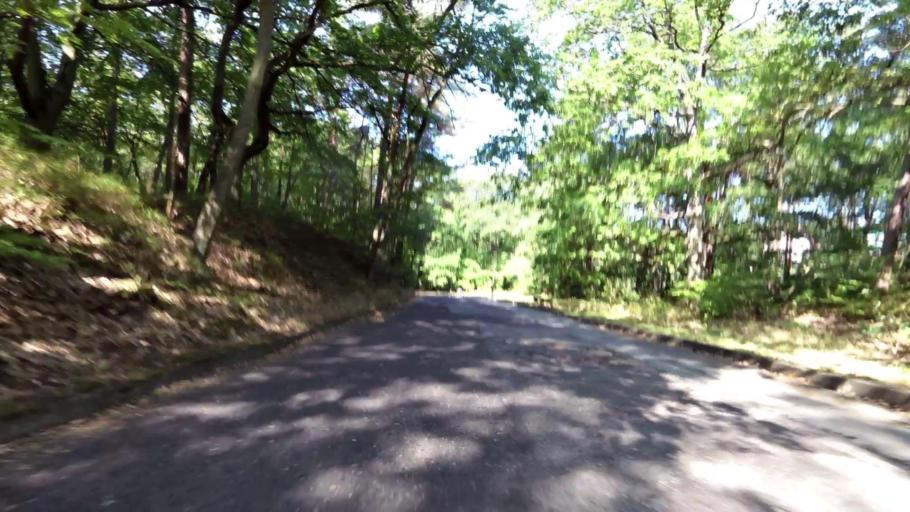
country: PL
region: West Pomeranian Voivodeship
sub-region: Powiat kamienski
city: Miedzyzdroje
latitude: 53.9243
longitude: 14.4603
